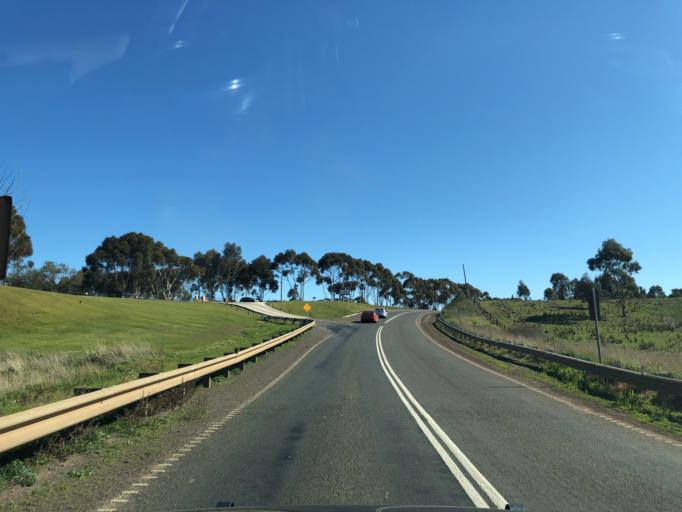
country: AU
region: Victoria
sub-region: Hume
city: Diggers Rest
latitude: -37.6260
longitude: 144.6682
